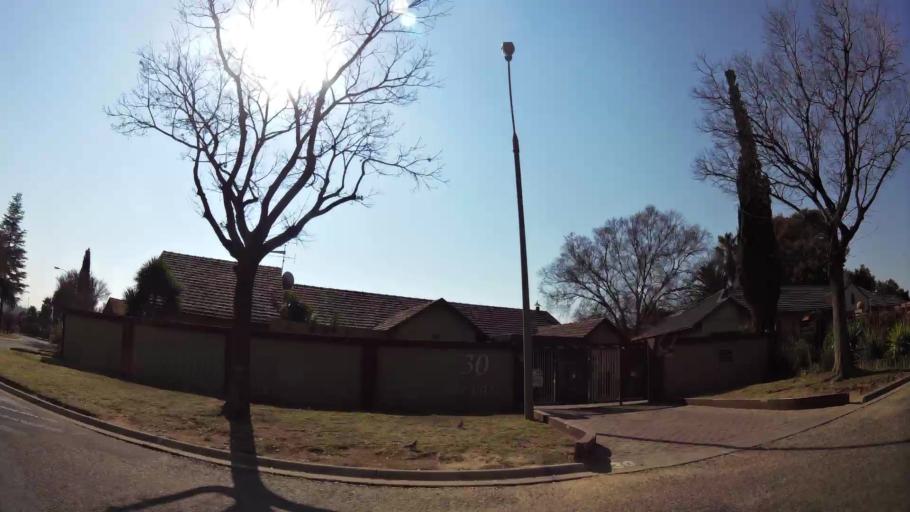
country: ZA
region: Gauteng
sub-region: Ekurhuleni Metropolitan Municipality
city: Boksburg
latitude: -26.2441
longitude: 28.2753
